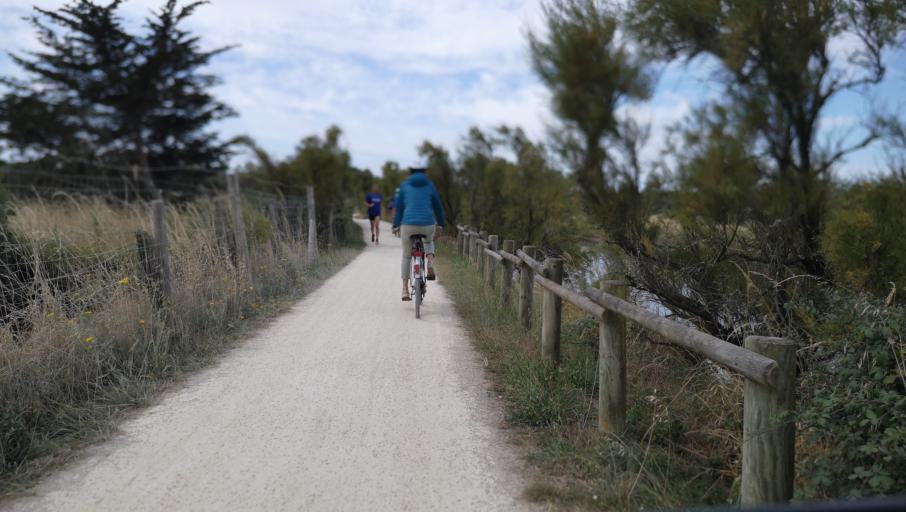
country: FR
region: Pays de la Loire
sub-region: Departement de la Vendee
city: Olonne-sur-Mer
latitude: 46.5336
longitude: -1.8064
